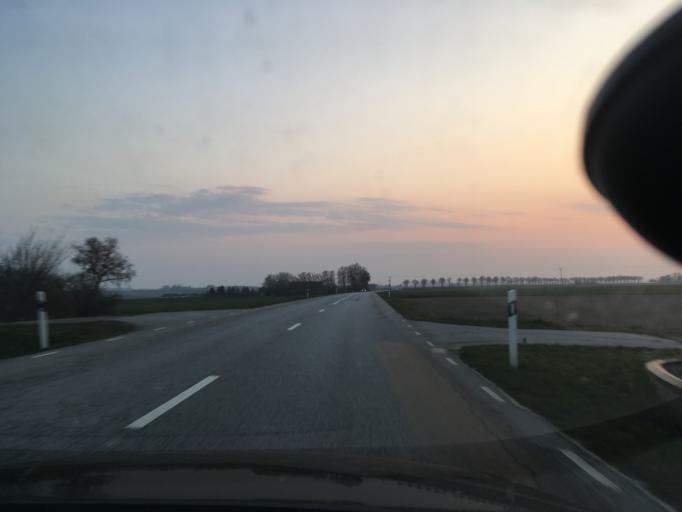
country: SE
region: Skane
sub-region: Ystads Kommun
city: Kopingebro
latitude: 55.4670
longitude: 14.0398
